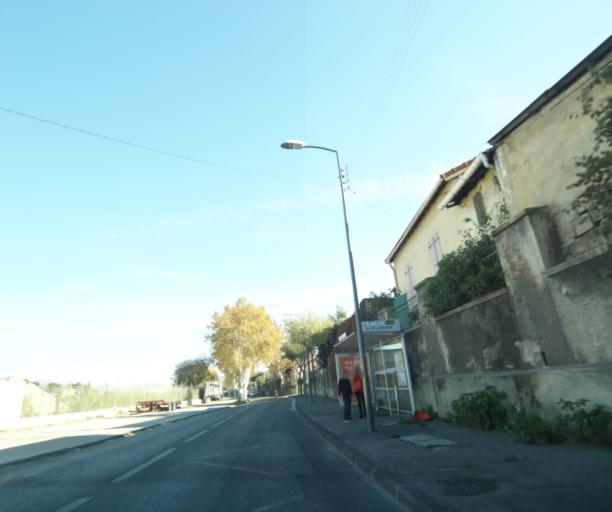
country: FR
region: Provence-Alpes-Cote d'Azur
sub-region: Departement des Bouches-du-Rhone
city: La Penne-sur-Huveaune
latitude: 43.2845
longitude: 5.4884
